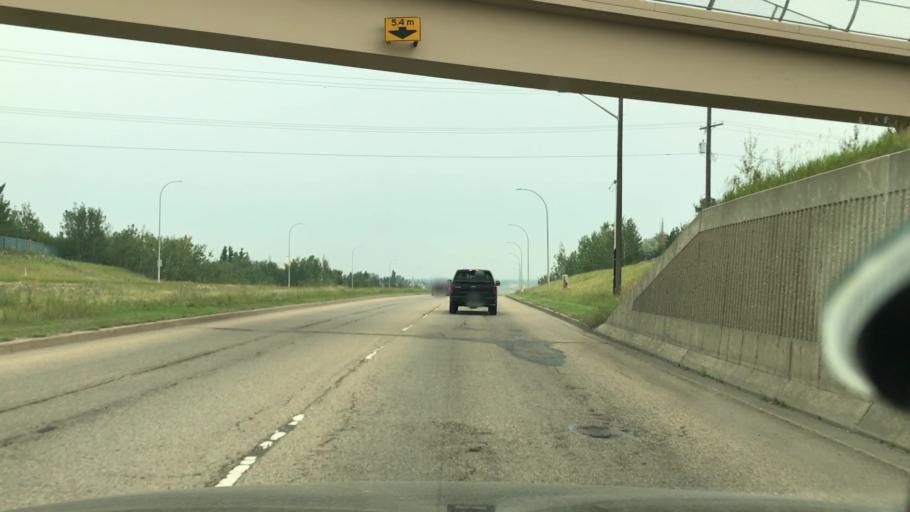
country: CA
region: Alberta
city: Edmonton
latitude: 53.4615
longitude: -113.5870
